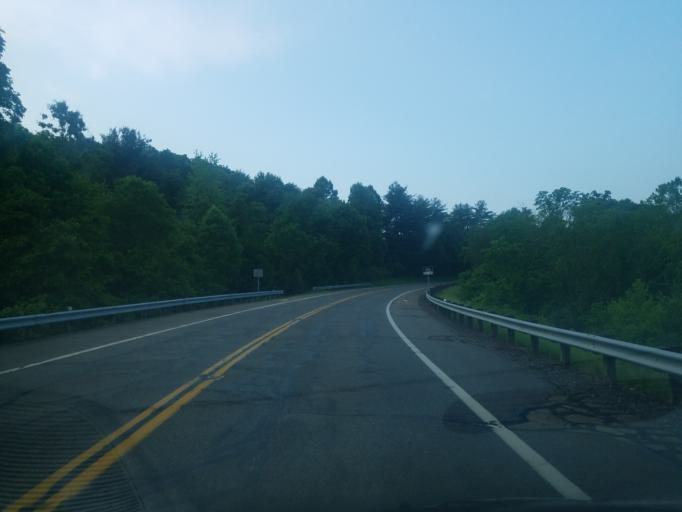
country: US
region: Ohio
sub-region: Tuscarawas County
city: Rockford
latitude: 40.5414
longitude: -81.2451
